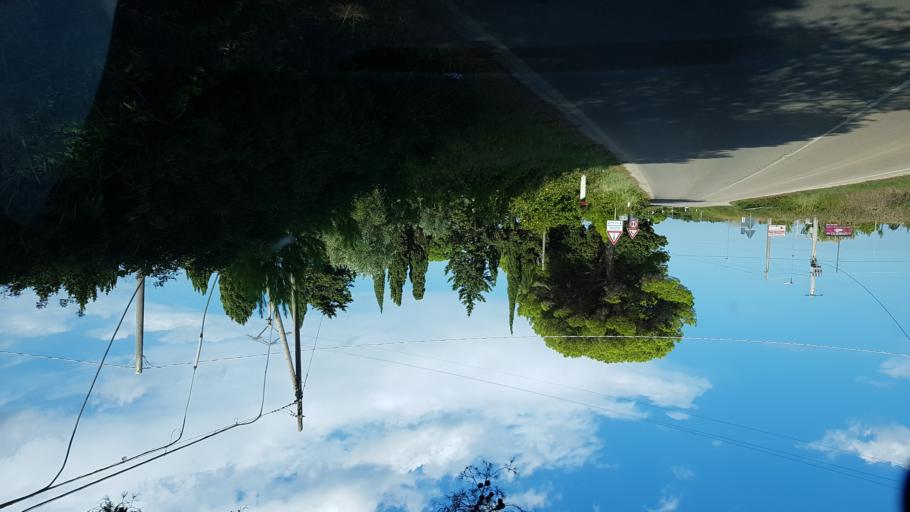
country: IT
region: Apulia
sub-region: Provincia di Lecce
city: Borgagne
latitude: 40.2271
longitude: 18.4421
